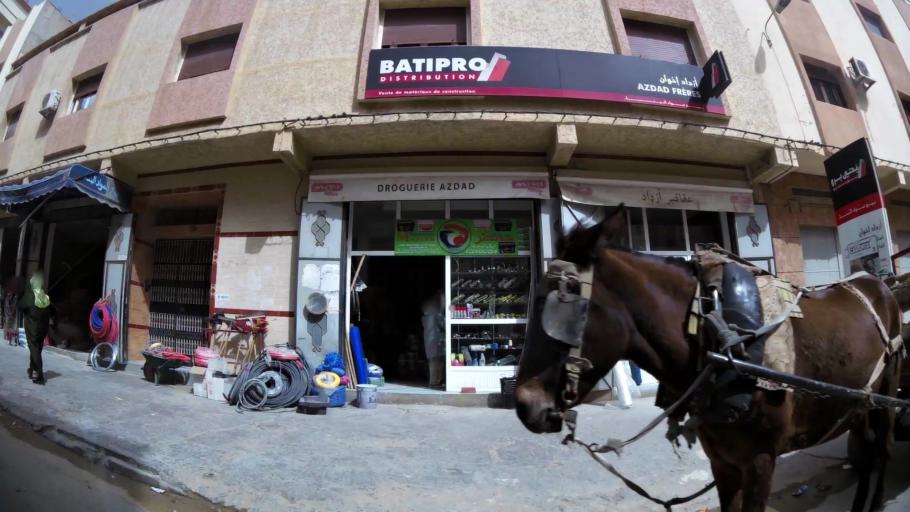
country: MA
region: Oriental
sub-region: Nador
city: Nador
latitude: 35.1607
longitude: -2.9335
